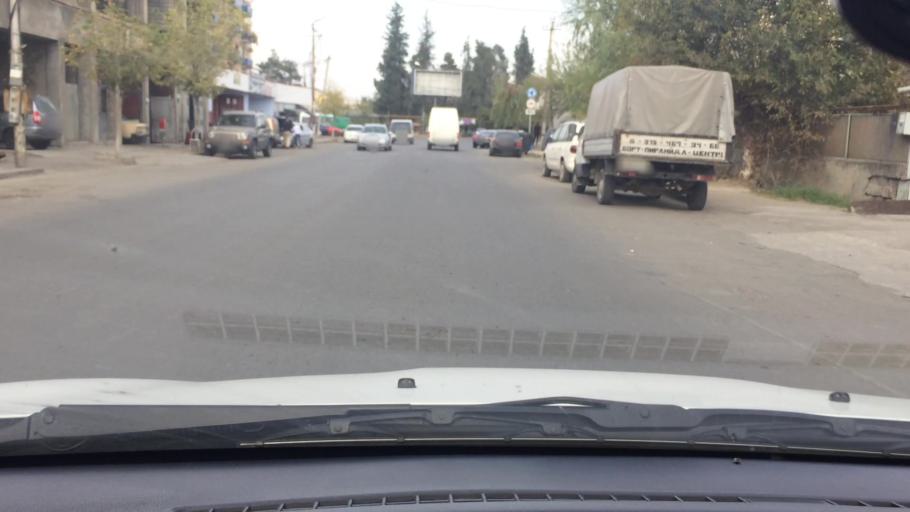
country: GE
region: Kvemo Kartli
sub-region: Marneuli
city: Marneuli
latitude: 41.4670
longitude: 44.8174
